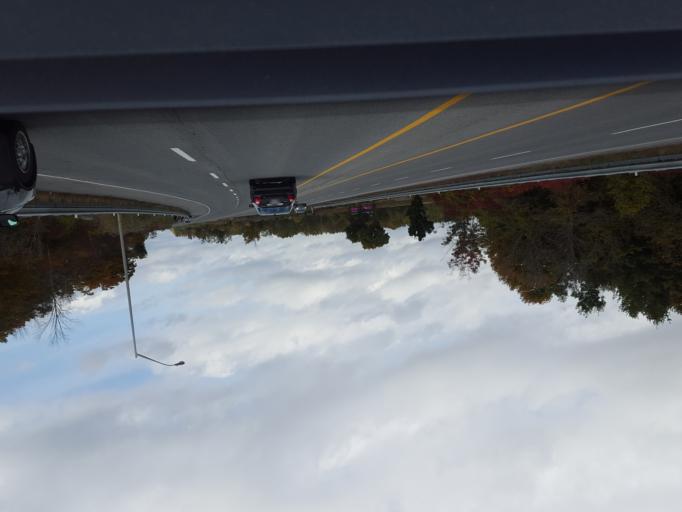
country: CA
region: Ontario
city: Pickering
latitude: 43.8742
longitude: -79.1337
